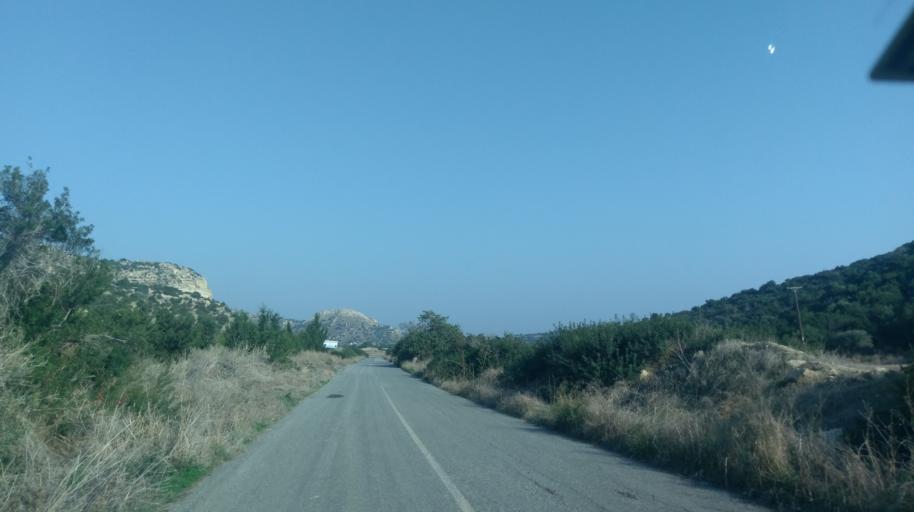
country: CY
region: Ammochostos
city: Rizokarpaso
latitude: 35.5130
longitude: 34.2881
